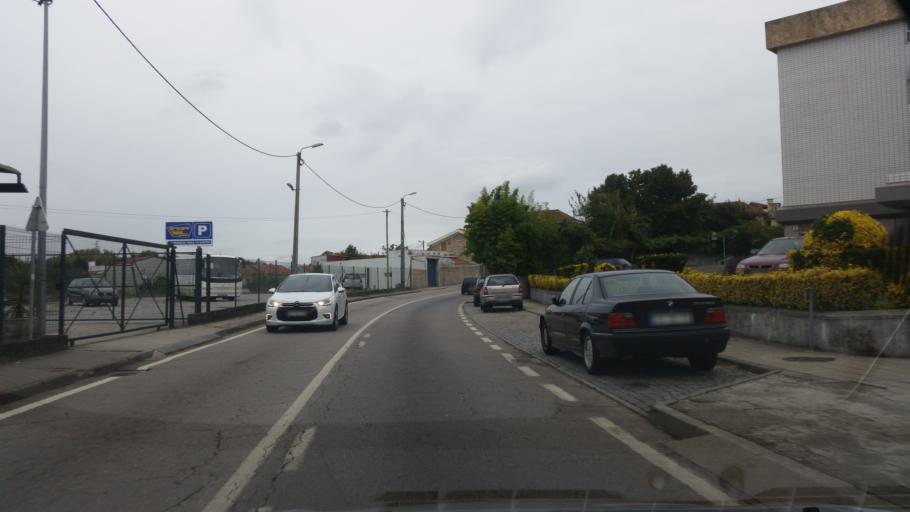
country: PT
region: Porto
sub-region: Valongo
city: Ermesinde
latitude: 41.2210
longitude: -8.5585
